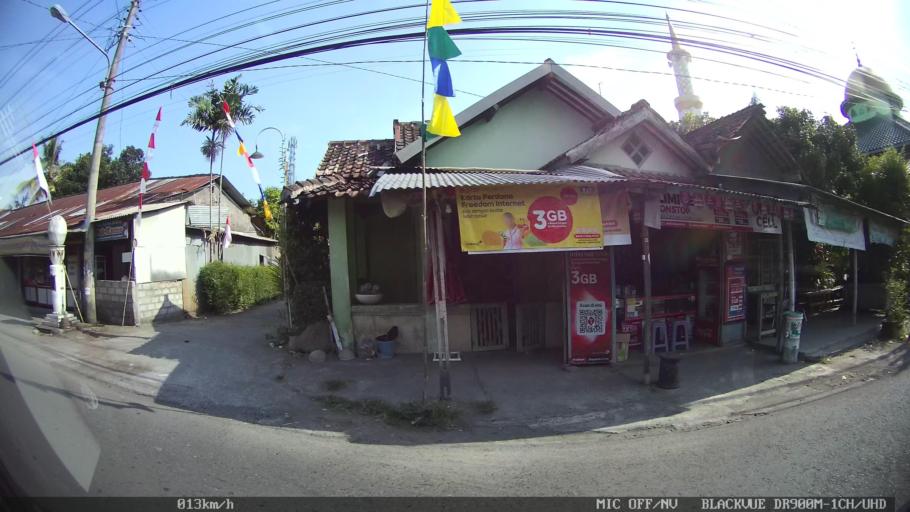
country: ID
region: Daerah Istimewa Yogyakarta
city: Kasihan
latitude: -7.8427
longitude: 110.3326
